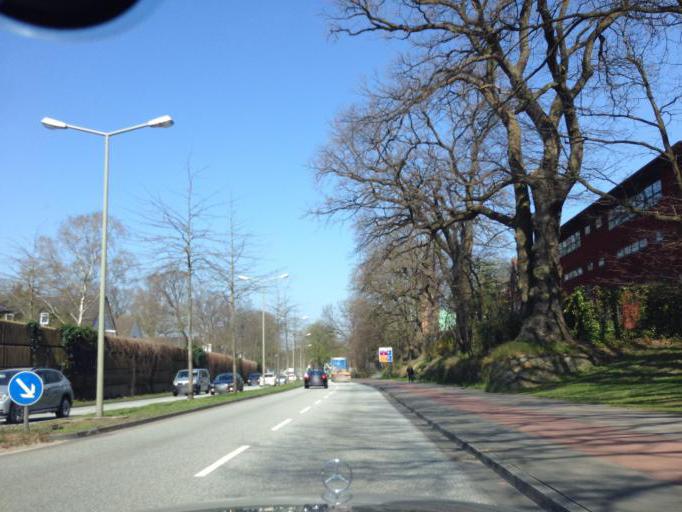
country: DE
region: Hamburg
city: Alsterdorf
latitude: 53.6114
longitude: 10.0229
